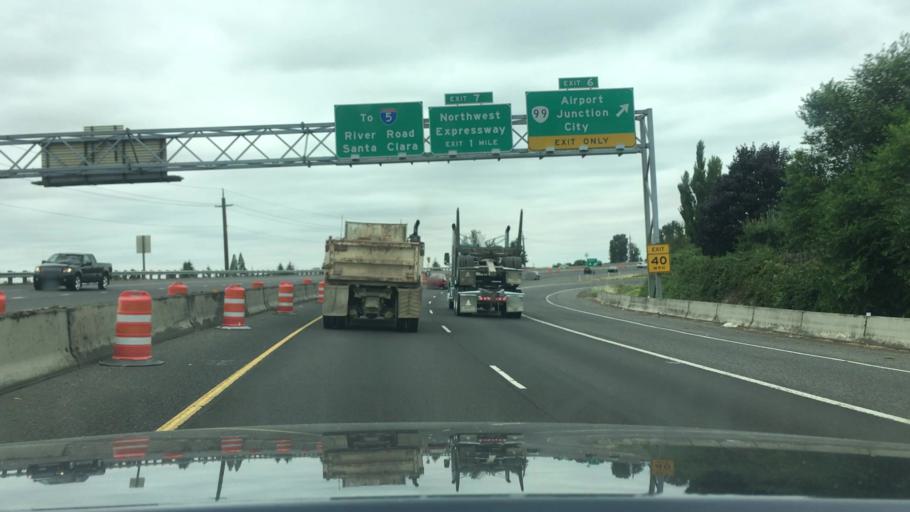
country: US
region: Oregon
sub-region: Lane County
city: Eugene
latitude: 44.0931
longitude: -123.1707
